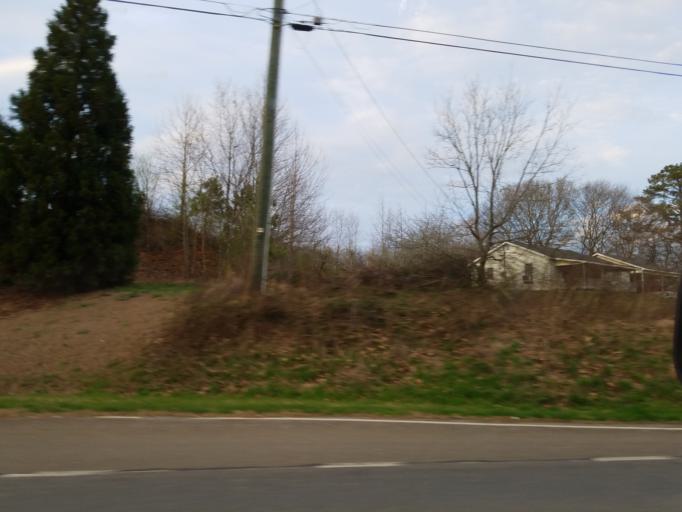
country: US
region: Georgia
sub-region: Pickens County
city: Jasper
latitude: 34.4688
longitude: -84.5008
